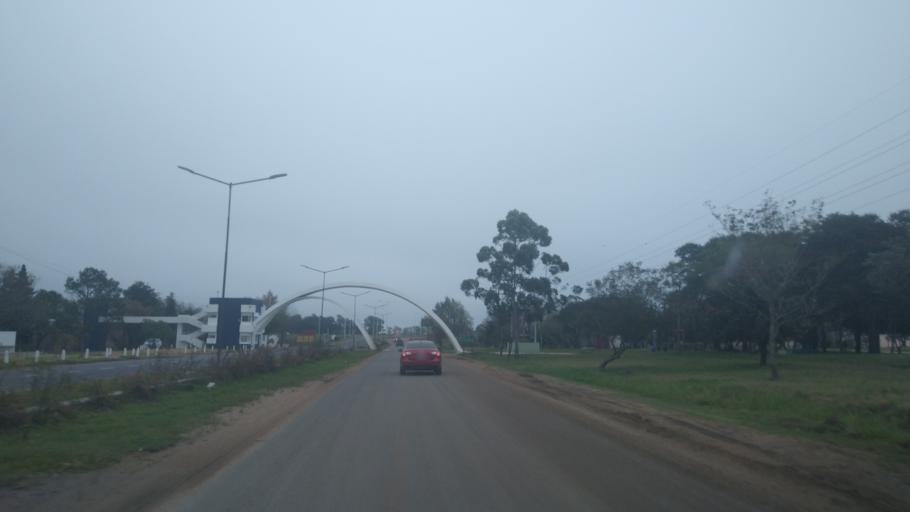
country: AR
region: Entre Rios
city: Chajari
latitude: -30.7620
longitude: -58.0157
